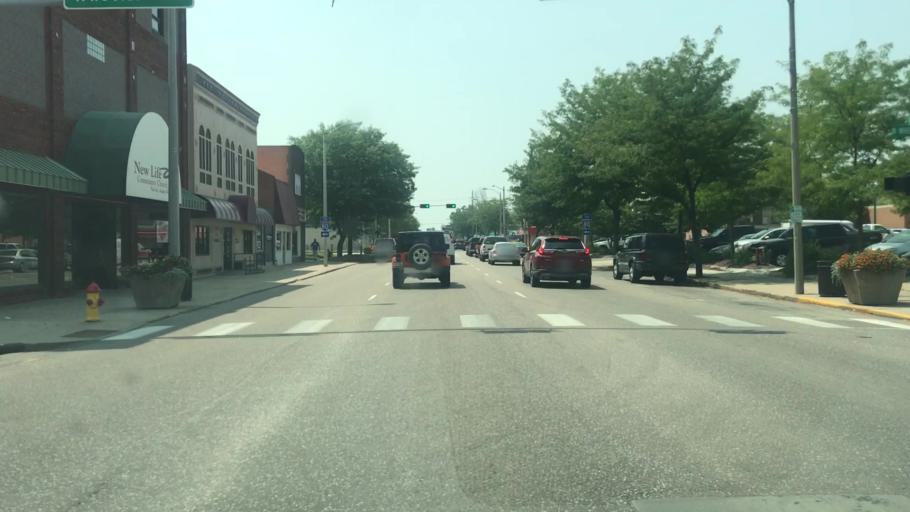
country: US
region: Nebraska
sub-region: Hall County
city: Grand Island
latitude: 40.9241
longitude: -98.3415
